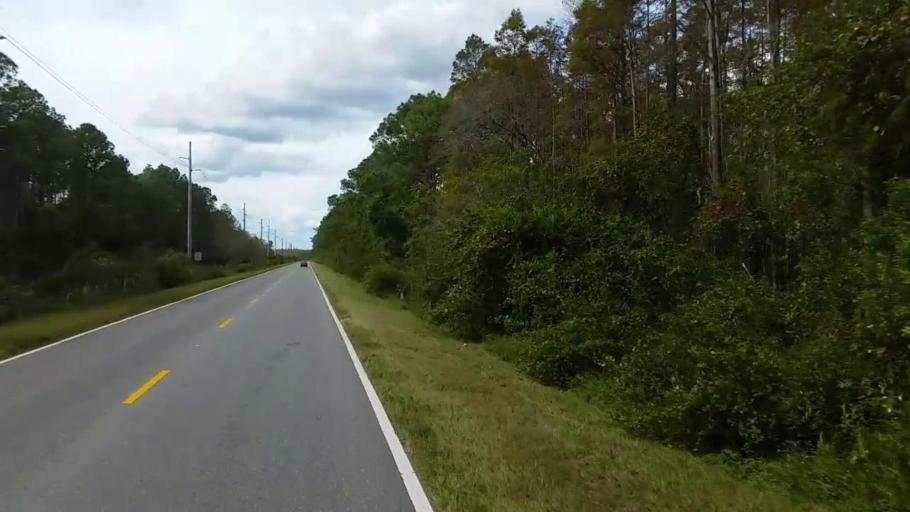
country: US
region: Florida
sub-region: Lake County
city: Four Corners
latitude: 28.3700
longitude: -81.7121
